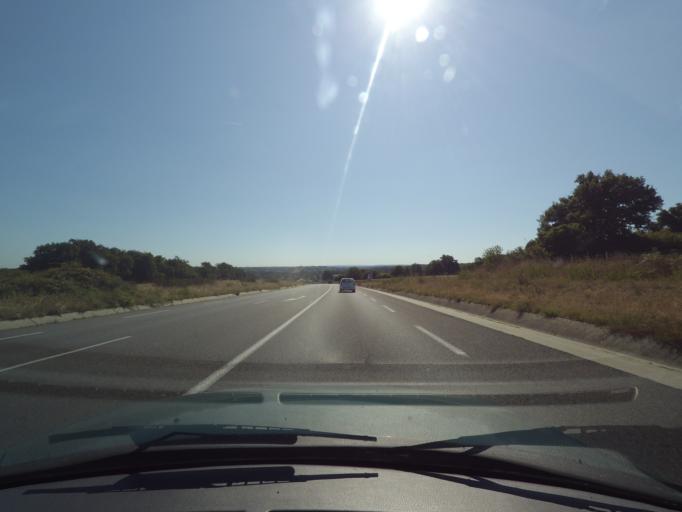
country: FR
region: Limousin
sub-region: Departement de la Haute-Vienne
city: Peyrat-de-Bellac
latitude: 46.1276
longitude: 0.9977
